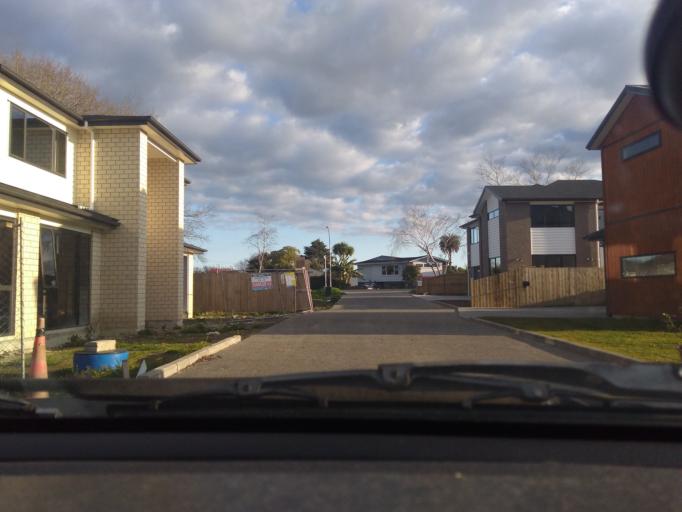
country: NZ
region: Auckland
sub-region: Auckland
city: Rosebank
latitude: -36.8887
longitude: 174.6773
